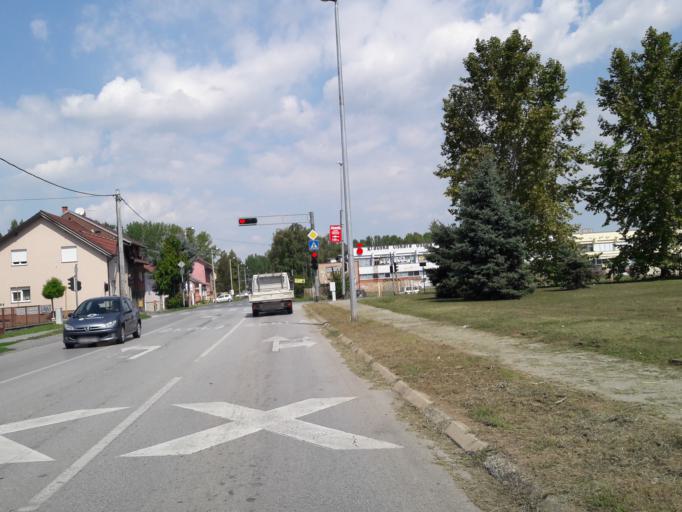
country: HR
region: Osjecko-Baranjska
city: Visnjevac
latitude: 45.5629
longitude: 18.6360
